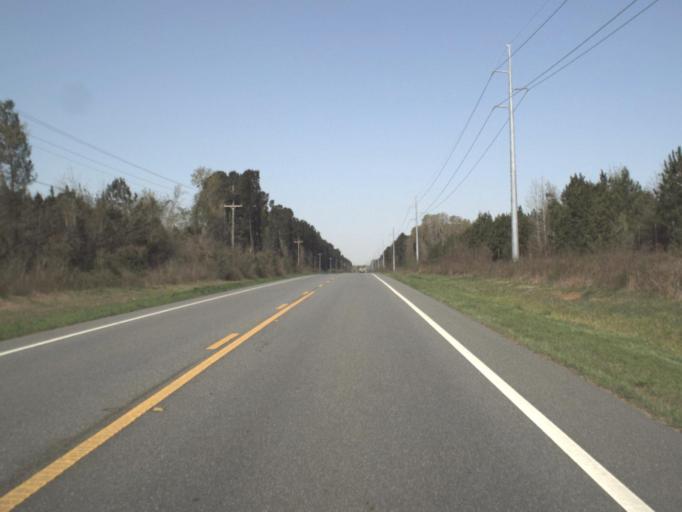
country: US
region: Alabama
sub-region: Houston County
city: Cottonwood
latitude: 30.9394
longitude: -85.3328
